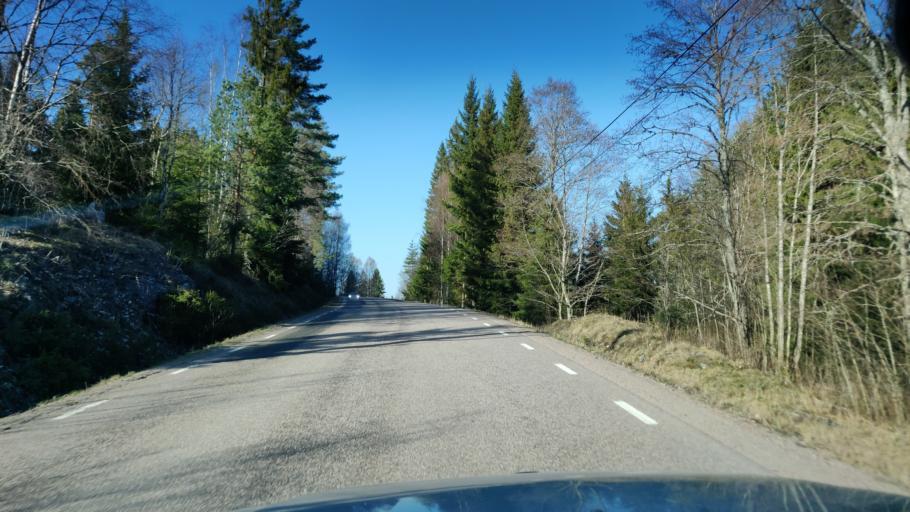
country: SE
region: Vaermland
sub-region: Sunne Kommun
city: Sunne
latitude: 59.9877
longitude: 13.2698
